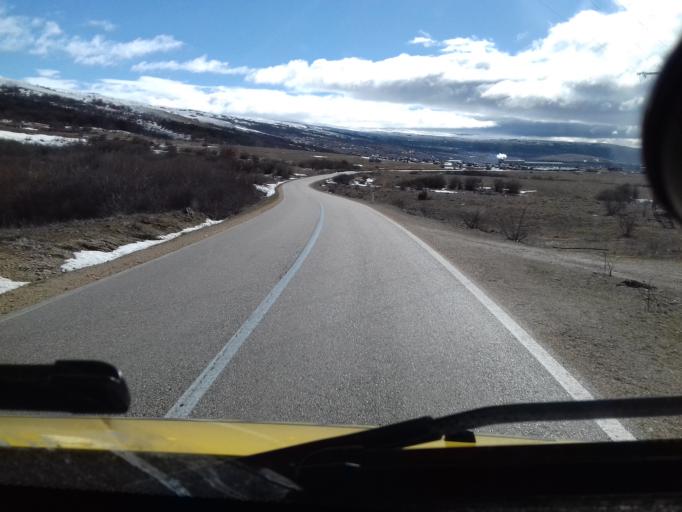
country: BA
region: Federation of Bosnia and Herzegovina
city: Tomislavgrad
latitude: 43.7750
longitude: 17.2298
